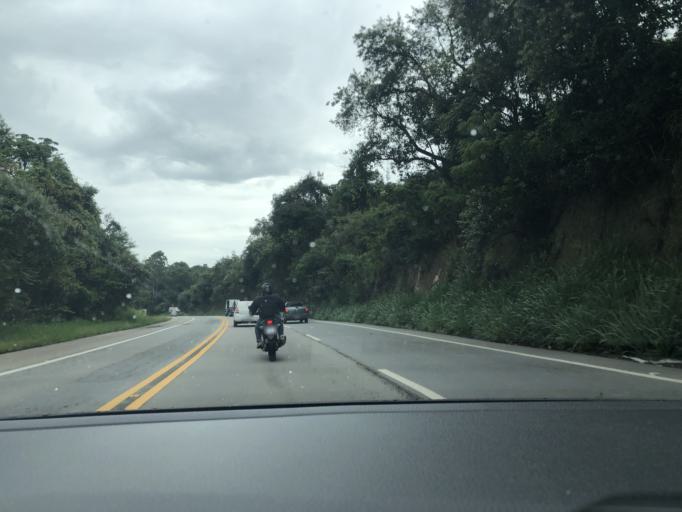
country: BR
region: Sao Paulo
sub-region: Jarinu
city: Jarinu
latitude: -23.1572
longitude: -46.7476
